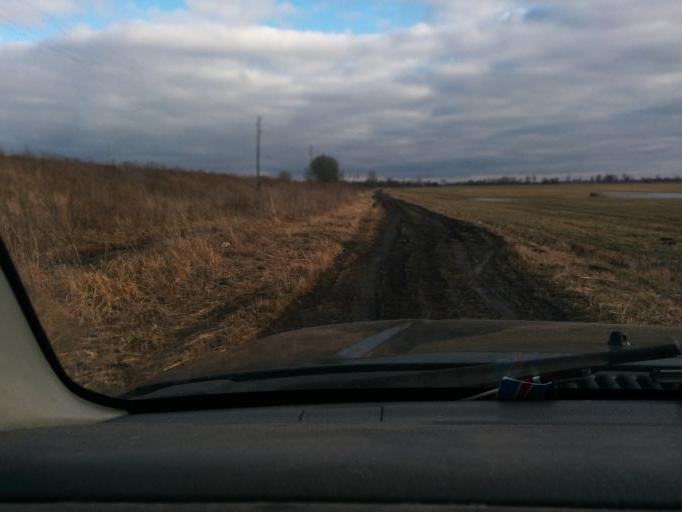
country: LV
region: Jelgava
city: Jelgava
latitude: 56.6911
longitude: 23.6855
